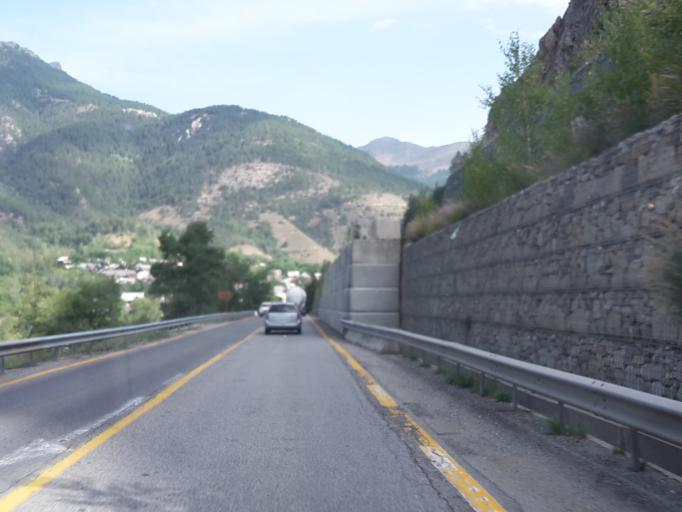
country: FR
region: Provence-Alpes-Cote d'Azur
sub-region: Departement des Hautes-Alpes
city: Saint-Martin-de-Queyrieres
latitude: 44.8472
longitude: 6.5831
